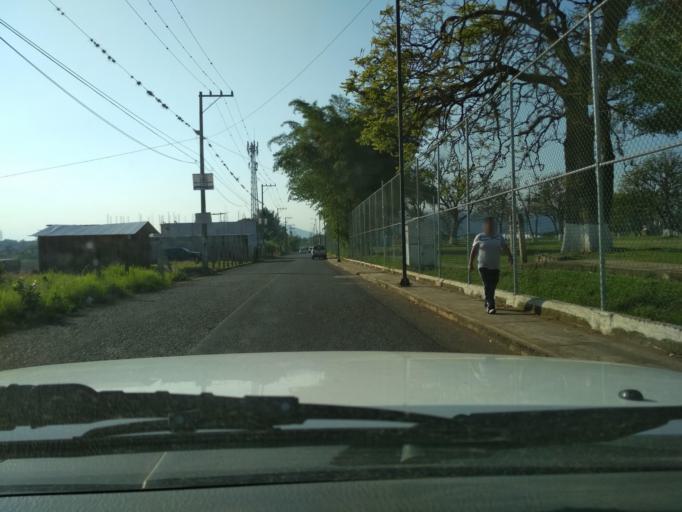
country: MX
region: Veracruz
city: Cordoba
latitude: 18.8698
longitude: -96.9282
